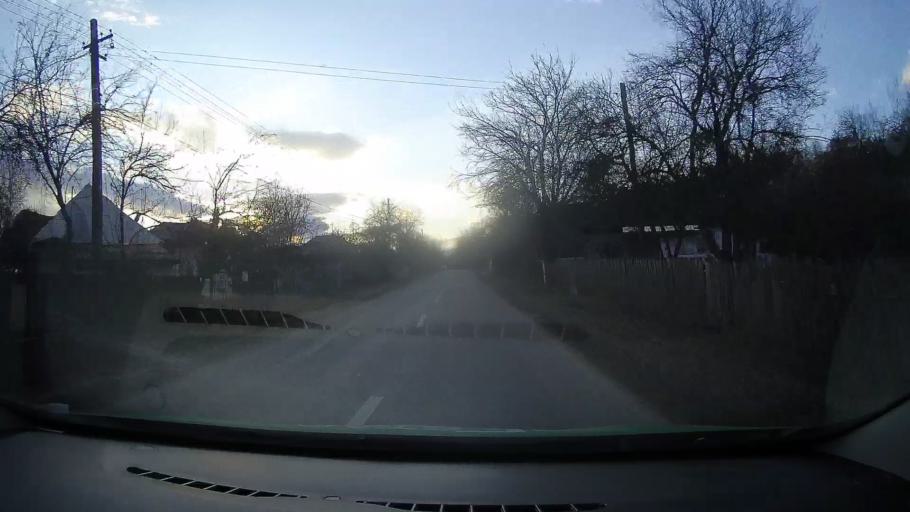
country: RO
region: Dambovita
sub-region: Comuna Gura Ocnitei
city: Adanca
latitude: 44.9357
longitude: 25.5929
